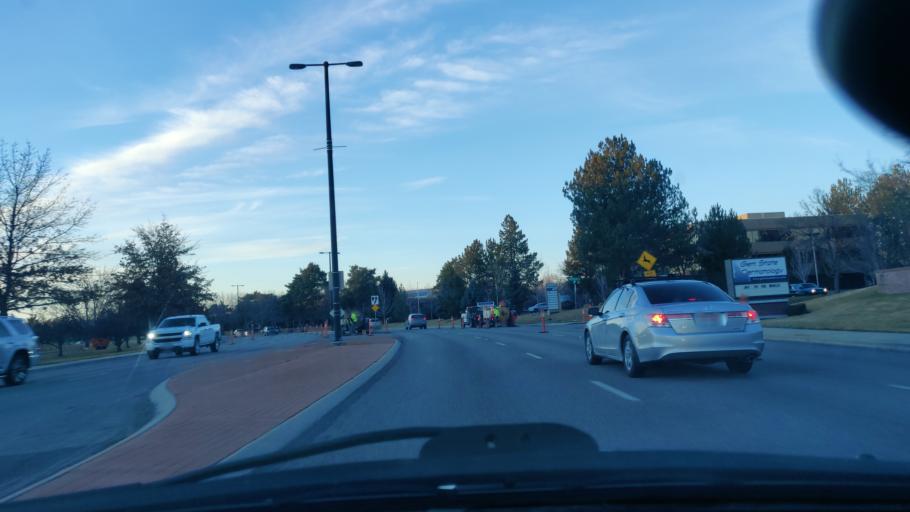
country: US
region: Idaho
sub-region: Ada County
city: Boise
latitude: 43.5970
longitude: -116.1780
